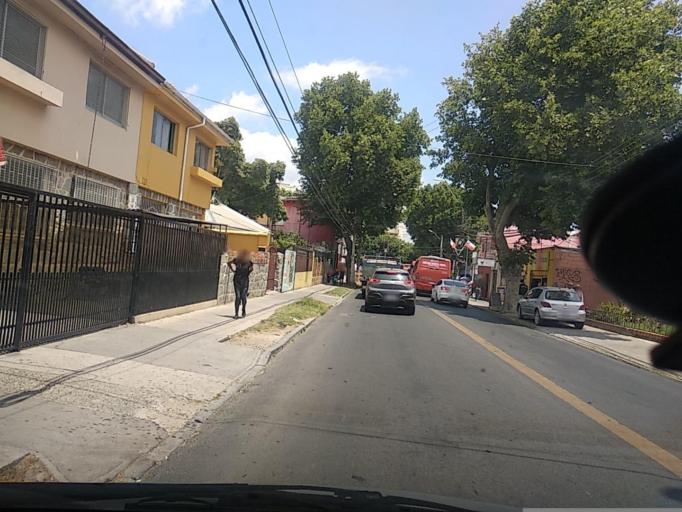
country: CL
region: Valparaiso
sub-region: Provincia de Marga Marga
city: Quilpue
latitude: -33.0458
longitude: -71.4397
